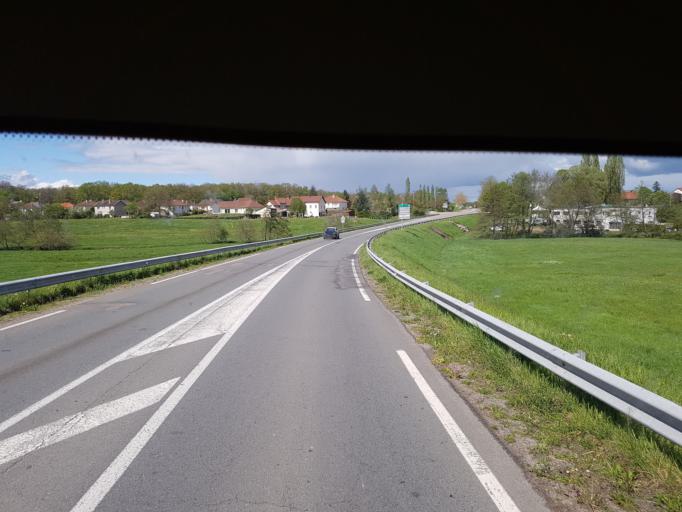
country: FR
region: Bourgogne
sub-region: Departement de Saone-et-Loire
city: Etang-sur-Arroux
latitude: 46.8698
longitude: 4.1752
